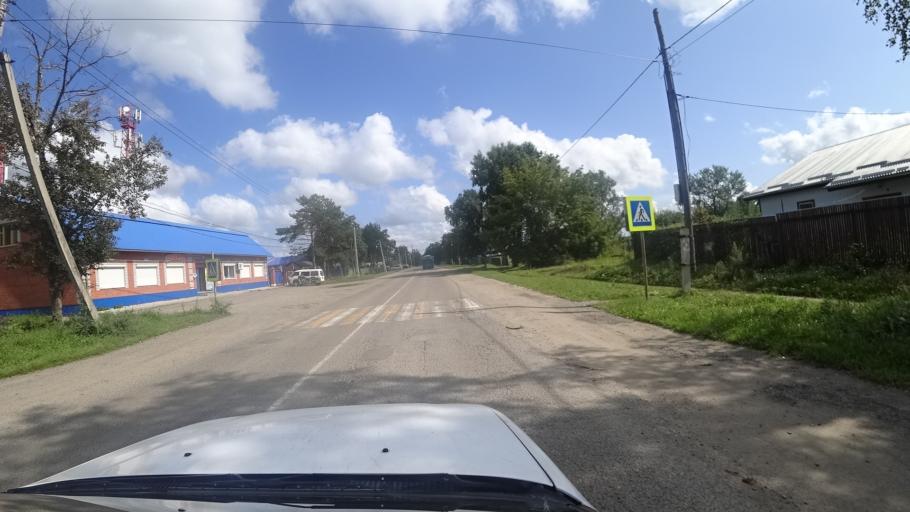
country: RU
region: Primorskiy
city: Dal'nerechensk
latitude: 45.9292
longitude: 133.7633
